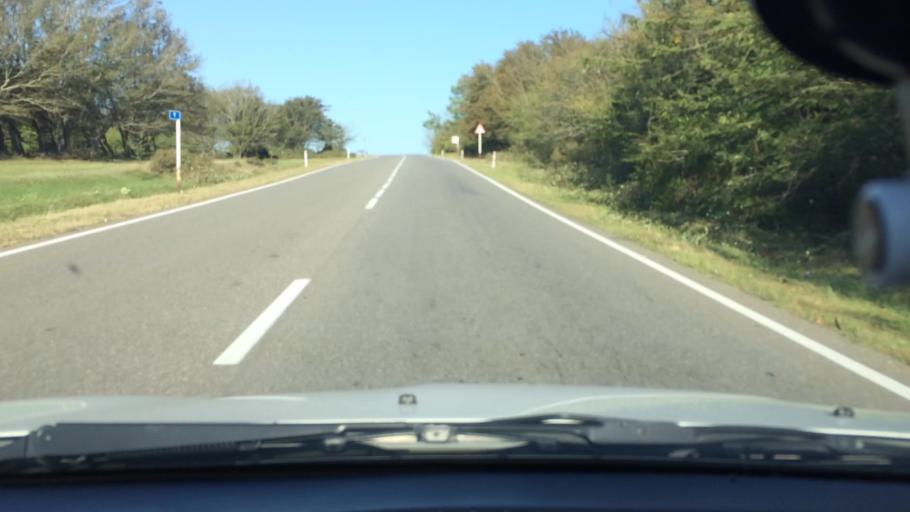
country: GE
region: Imereti
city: Kutaisi
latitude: 42.2509
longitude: 42.7529
